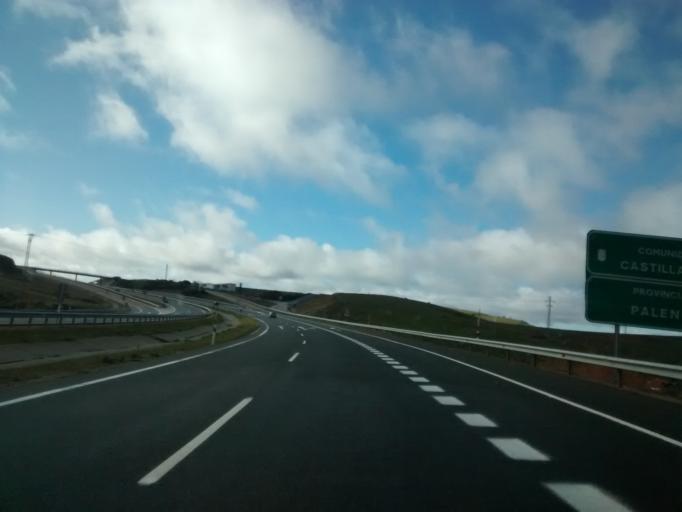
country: ES
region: Cantabria
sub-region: Provincia de Cantabria
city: Mataporquera
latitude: 42.8714
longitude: -4.1490
